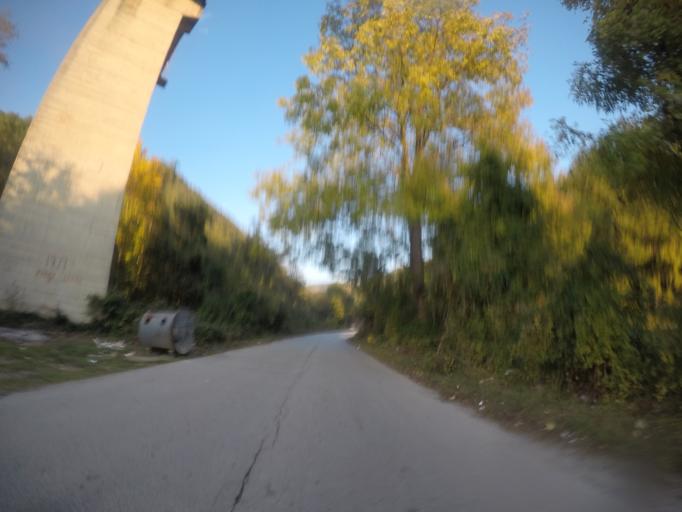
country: ME
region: Opstina Kolasin
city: Kolasin
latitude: 42.8305
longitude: 19.5498
